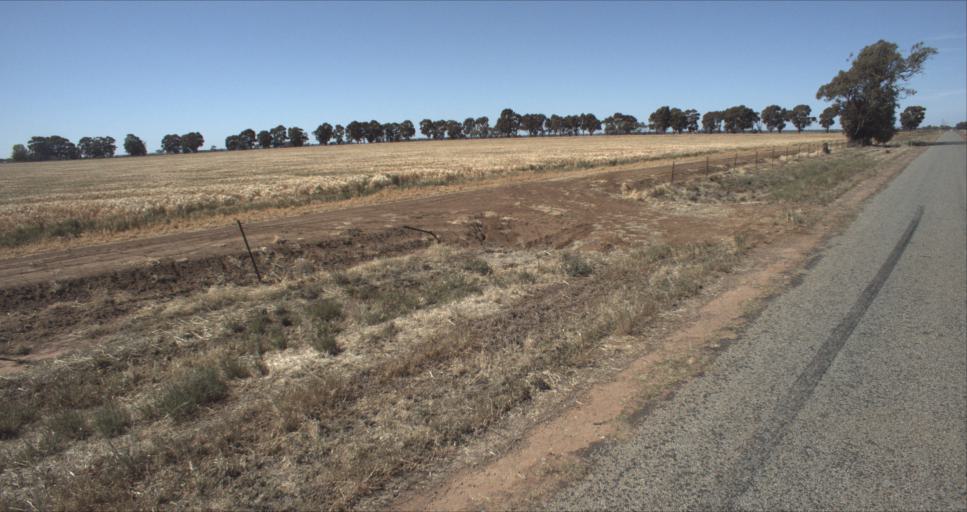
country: AU
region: New South Wales
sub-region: Leeton
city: Leeton
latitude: -34.5458
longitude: 146.3156
